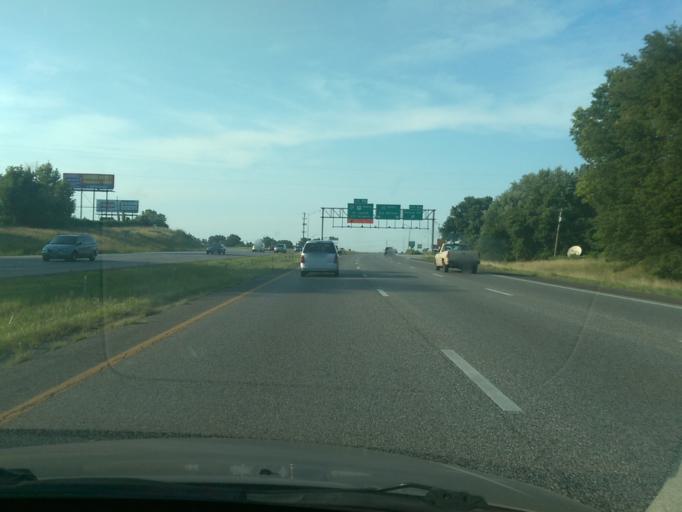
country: US
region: Missouri
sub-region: Clay County
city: North Kansas City
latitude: 39.1623
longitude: -94.5595
